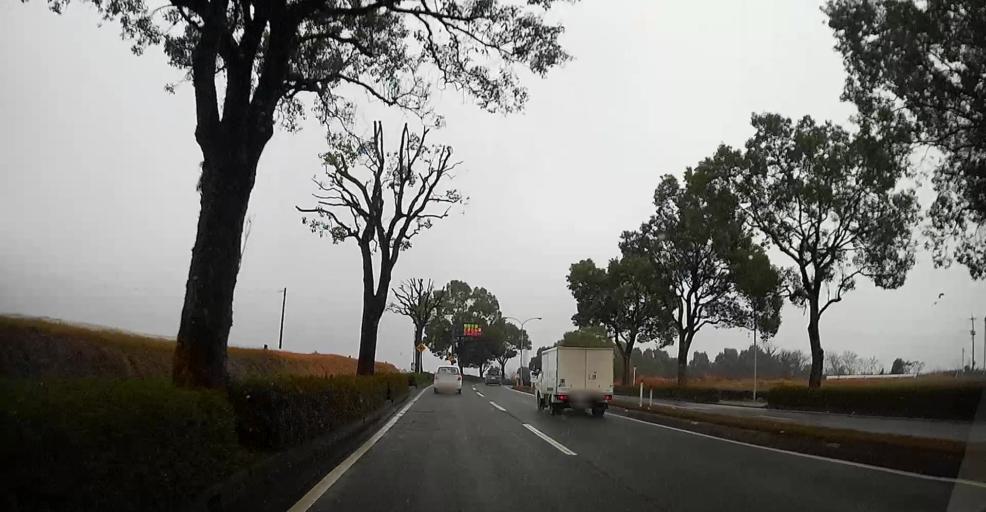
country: JP
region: Kumamoto
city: Ozu
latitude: 32.8271
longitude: 130.8591
